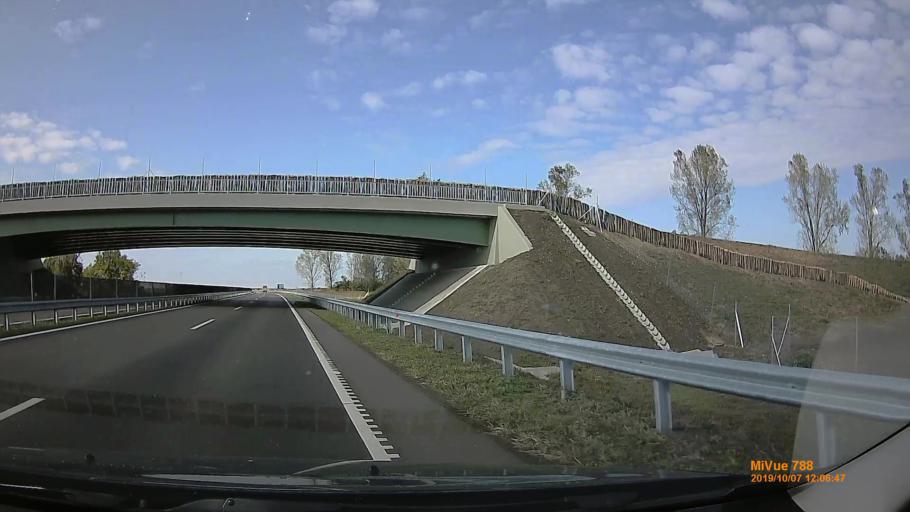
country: HU
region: Bekes
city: Bekesszentandras
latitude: 46.8254
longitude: 20.4889
